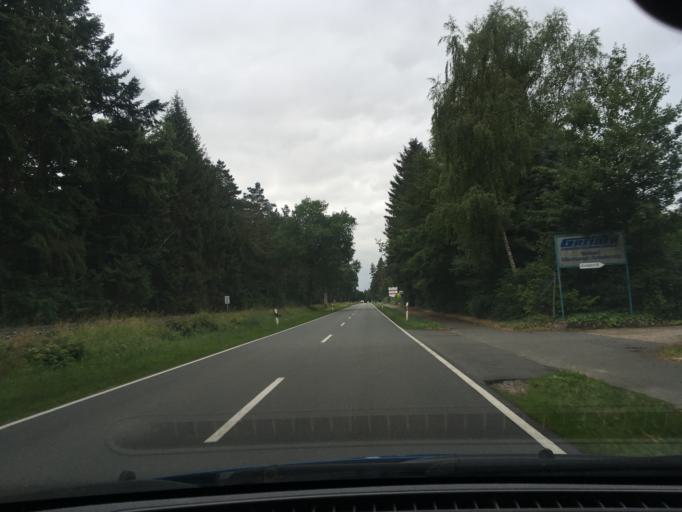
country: DE
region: Lower Saxony
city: Wulfsen
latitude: 53.2897
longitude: 10.1403
